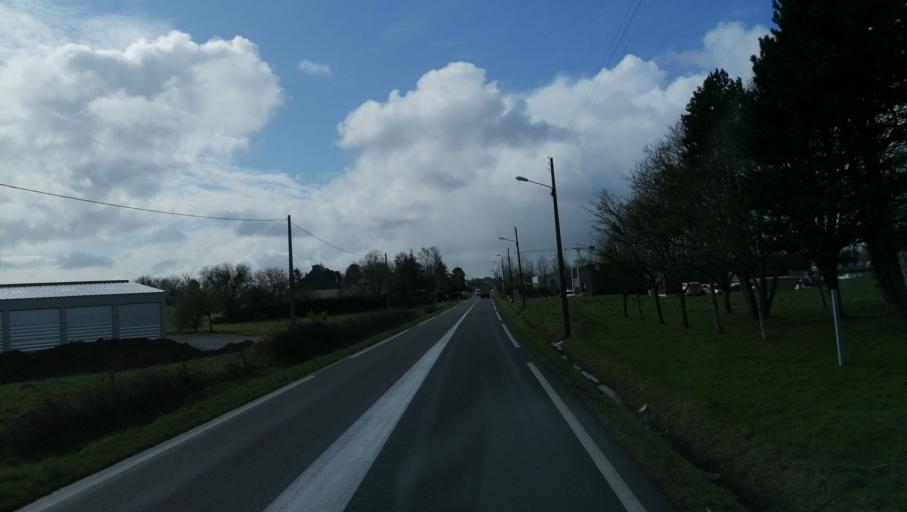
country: FR
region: Brittany
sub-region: Departement des Cotes-d'Armor
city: Ploufragan
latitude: 48.4795
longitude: -2.7955
